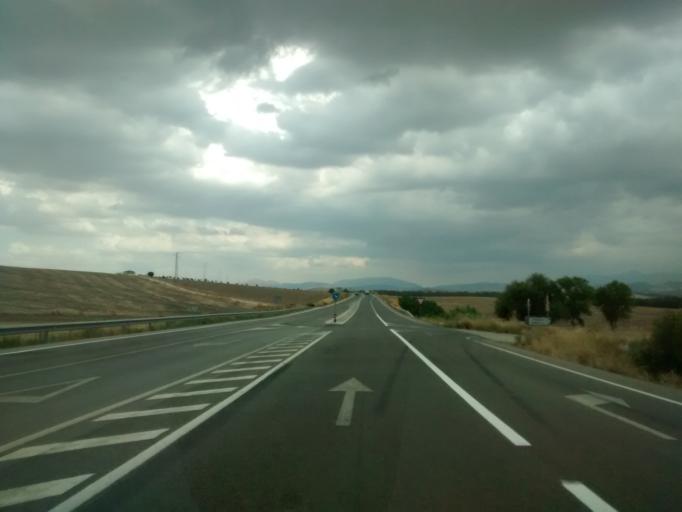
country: ES
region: Andalusia
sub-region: Provincia de Cadiz
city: Bornos
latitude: 36.8260
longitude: -5.7369
